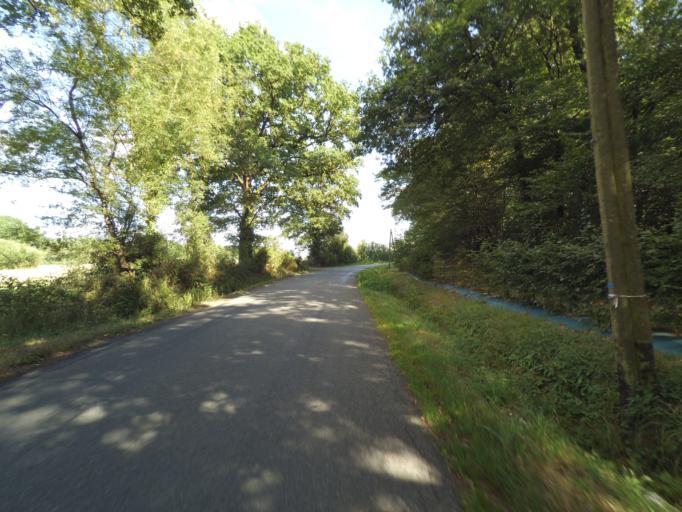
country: FR
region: Pays de la Loire
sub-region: Departement de la Loire-Atlantique
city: Vieillevigne
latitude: 46.9583
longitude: -1.4549
